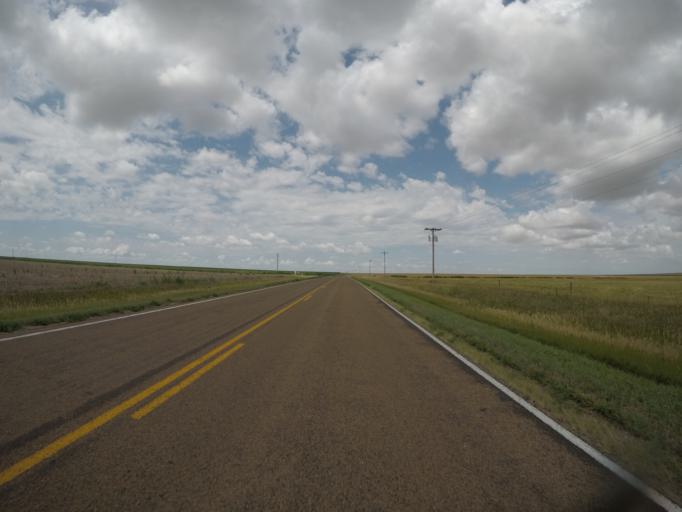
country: US
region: Kansas
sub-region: Rawlins County
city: Atwood
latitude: 39.9281
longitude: -101.0561
